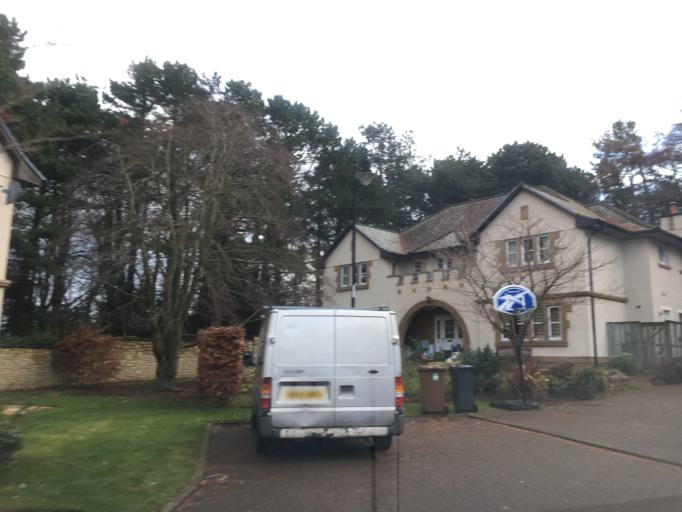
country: GB
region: Scotland
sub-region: Edinburgh
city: Colinton
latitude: 55.9142
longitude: -3.2238
